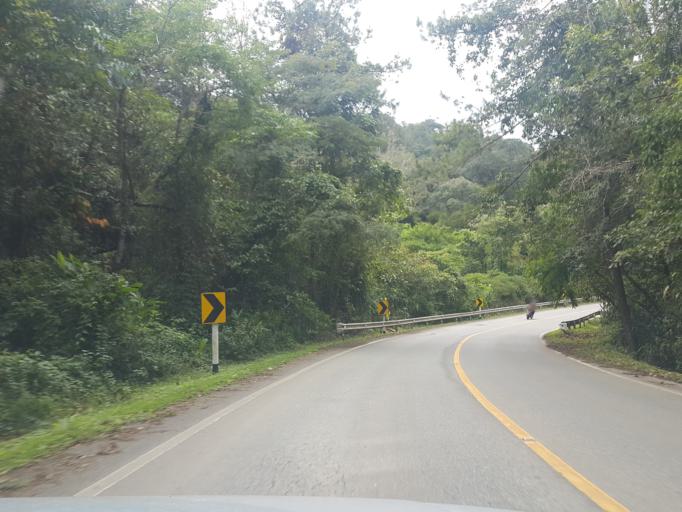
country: TH
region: Chiang Mai
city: Mae Chaem
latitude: 18.5184
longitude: 98.5012
